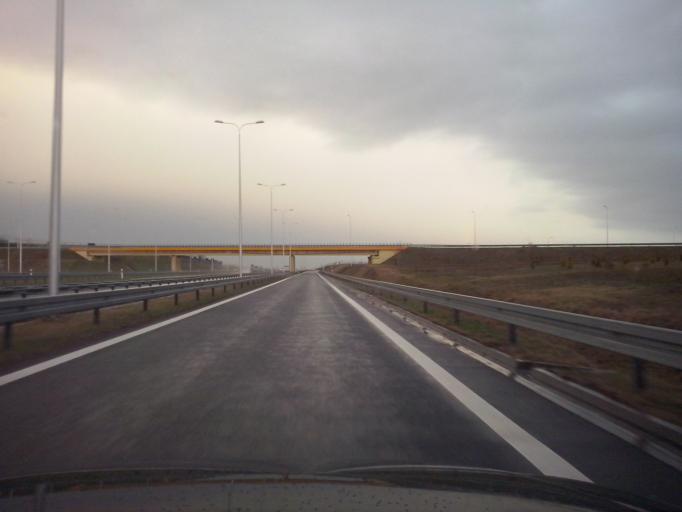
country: PL
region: Lublin Voivodeship
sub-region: Powiat lubelski
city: Jastkow
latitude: 51.2842
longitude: 22.4522
